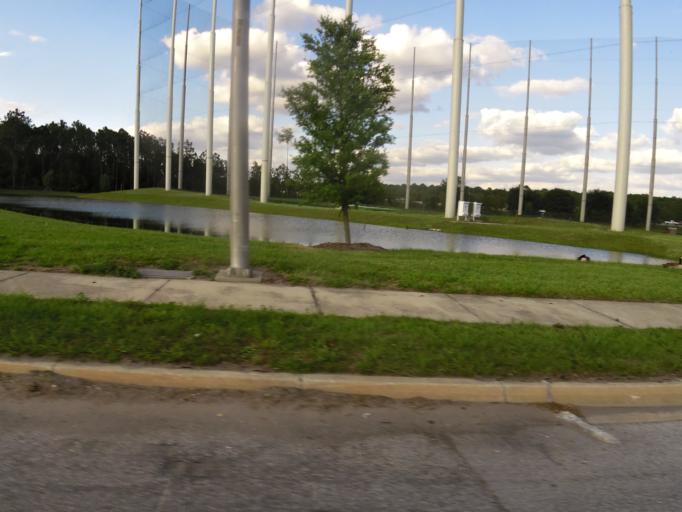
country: US
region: Florida
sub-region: Duval County
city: Jacksonville Beach
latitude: 30.2640
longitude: -81.5215
